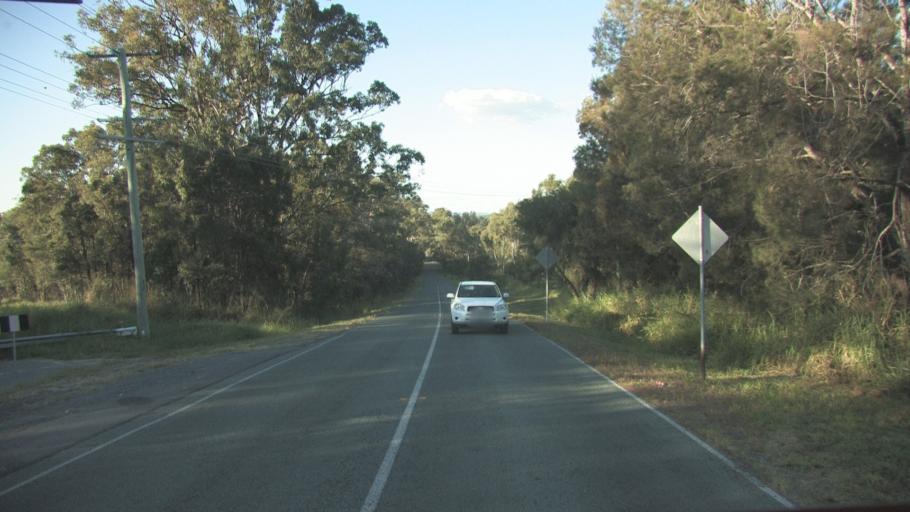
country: AU
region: Queensland
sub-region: Logan
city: Logan Reserve
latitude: -27.7239
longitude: 153.1056
